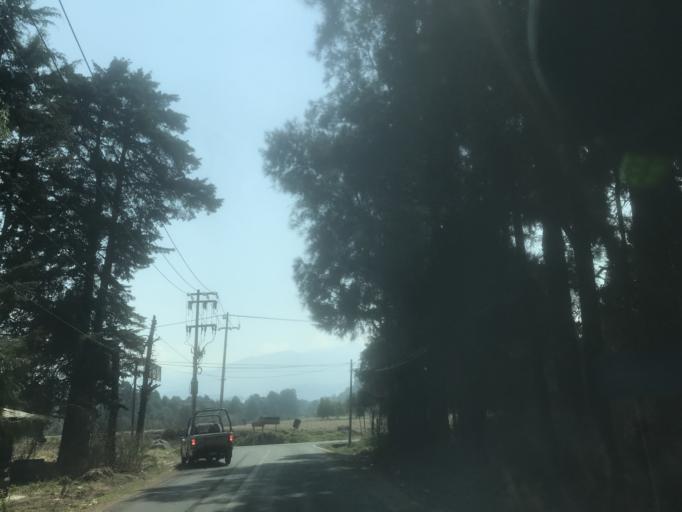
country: MX
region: Mexico
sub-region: Ecatzingo
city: San Marcos Tecomaxusco
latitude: 18.9999
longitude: -98.7685
